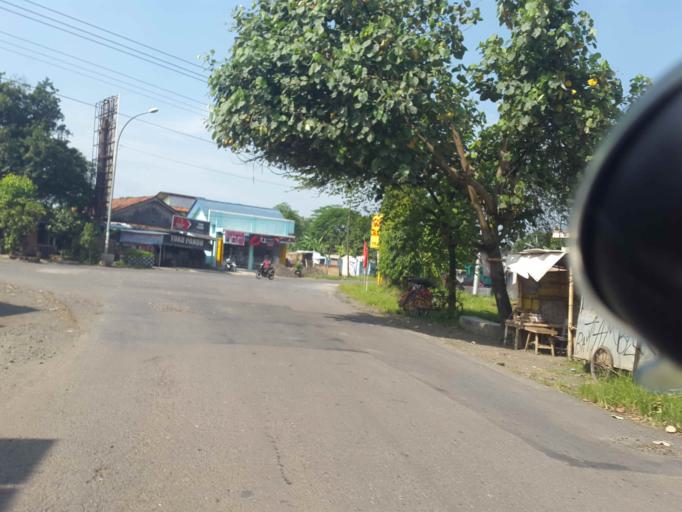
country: ID
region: Central Java
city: Wangon
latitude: -7.5151
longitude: 109.0483
